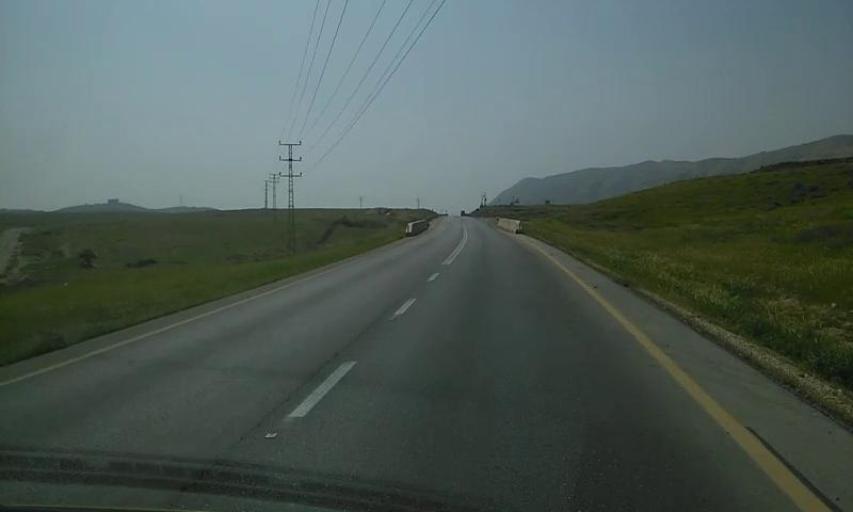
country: PS
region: West Bank
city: An Nuway`imah
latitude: 31.9086
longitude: 35.4227
